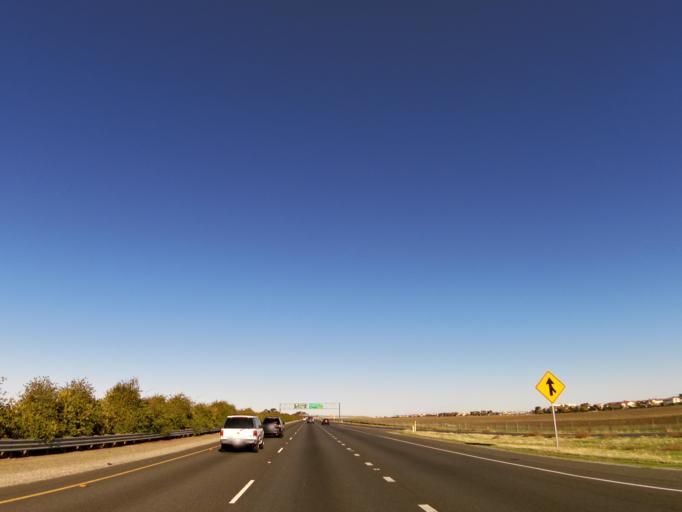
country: US
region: California
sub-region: Yolo County
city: West Sacramento
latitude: 38.6569
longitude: -121.5335
